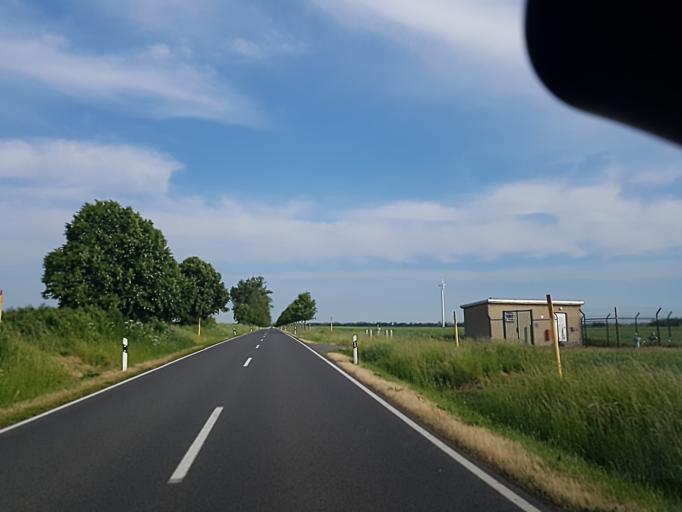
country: DE
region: Saxony-Anhalt
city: Kropstadt
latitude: 52.0070
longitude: 12.7666
